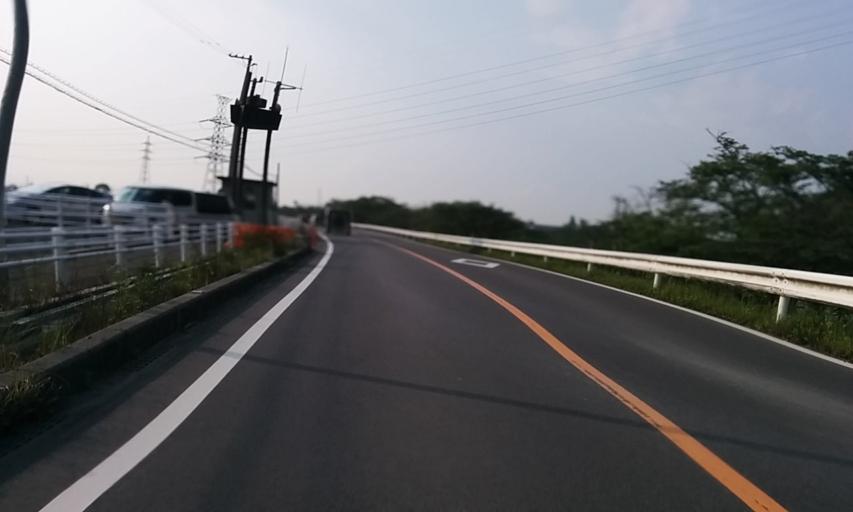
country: JP
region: Ehime
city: Saijo
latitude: 33.8951
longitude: 133.1942
